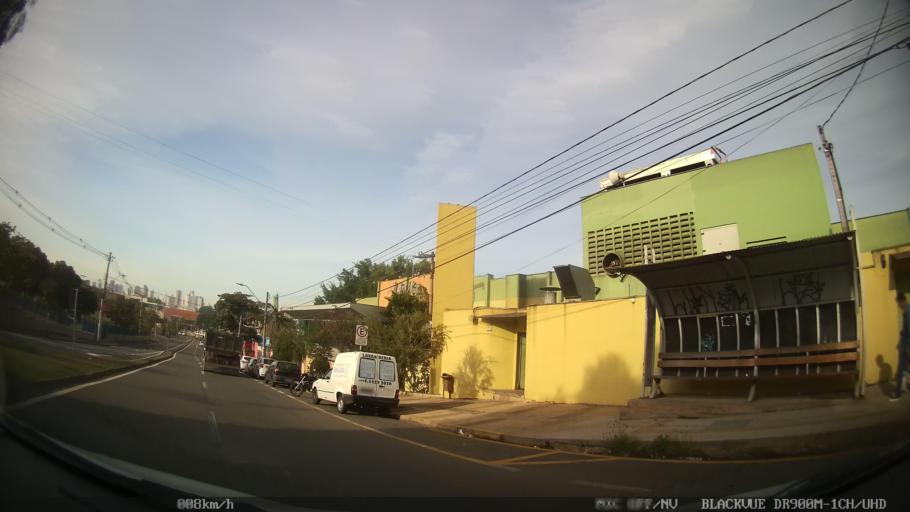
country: BR
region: Sao Paulo
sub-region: Piracicaba
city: Piracicaba
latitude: -22.7012
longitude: -47.6519
